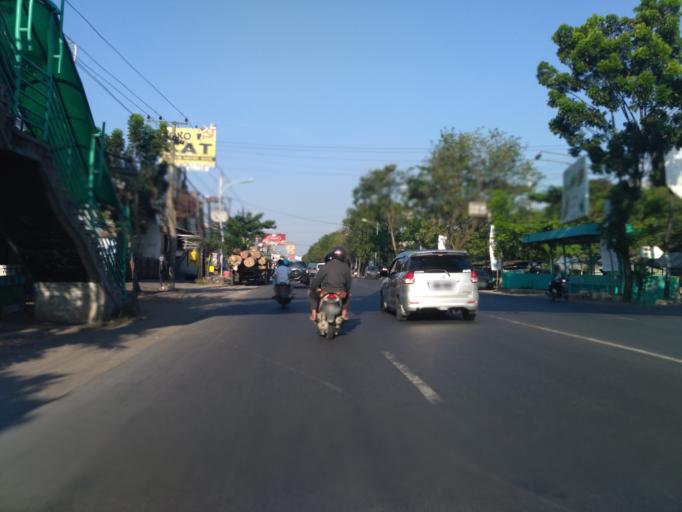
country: ID
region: Central Java
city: Semarang
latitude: -7.0077
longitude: 110.4614
